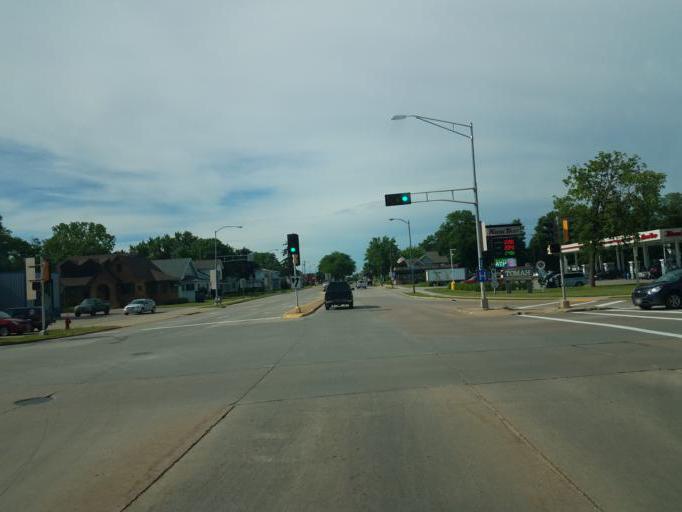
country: US
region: Wisconsin
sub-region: Monroe County
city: Tomah
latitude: 43.9717
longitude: -90.5047
